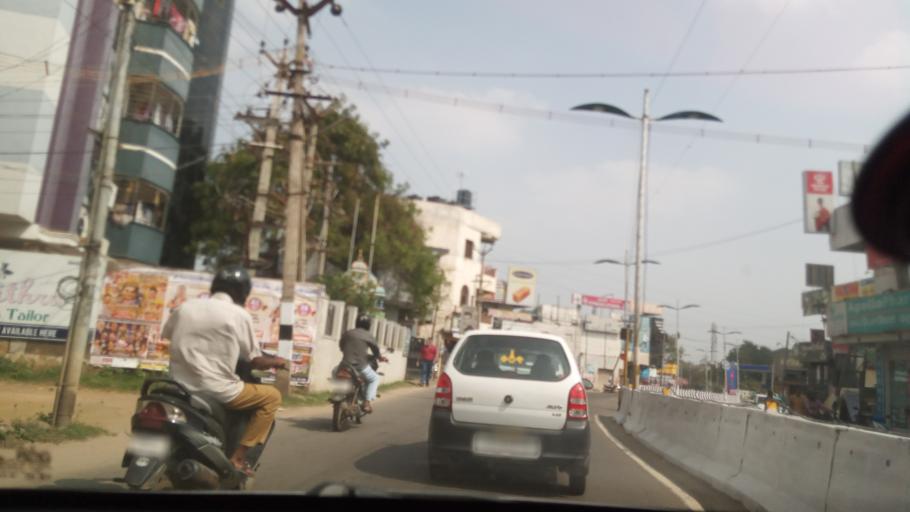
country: IN
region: Tamil Nadu
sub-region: Coimbatore
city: Perur
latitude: 11.0216
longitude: 76.9167
